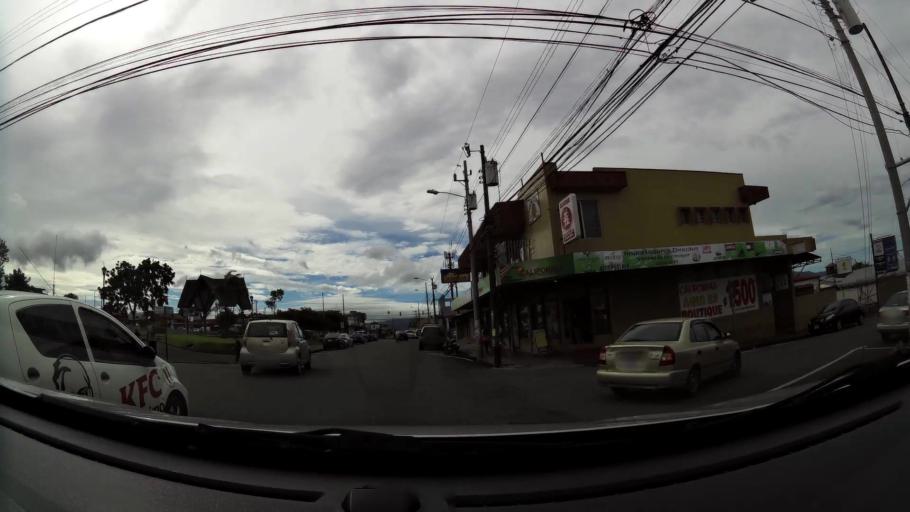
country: CR
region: San Jose
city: Ipis
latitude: 9.9767
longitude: -84.0082
